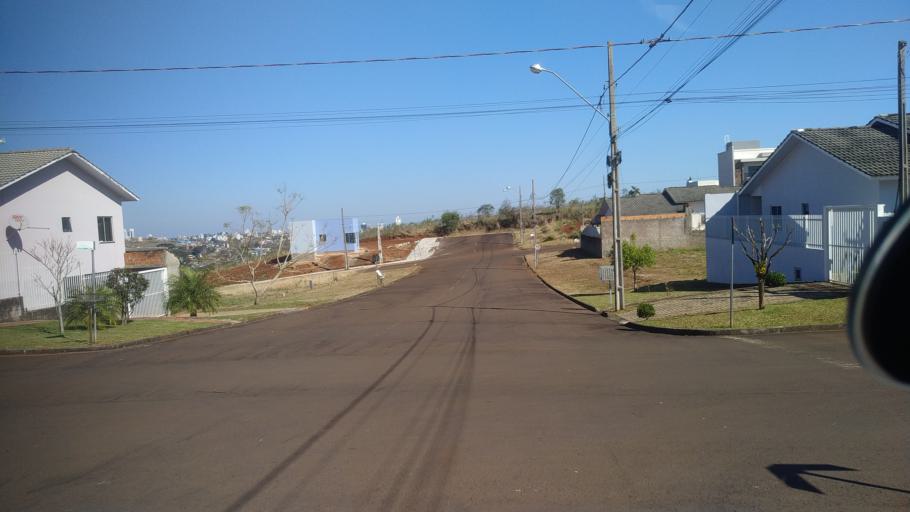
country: BR
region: Santa Catarina
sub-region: Chapeco
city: Chapeco
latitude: -27.0910
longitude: -52.5793
